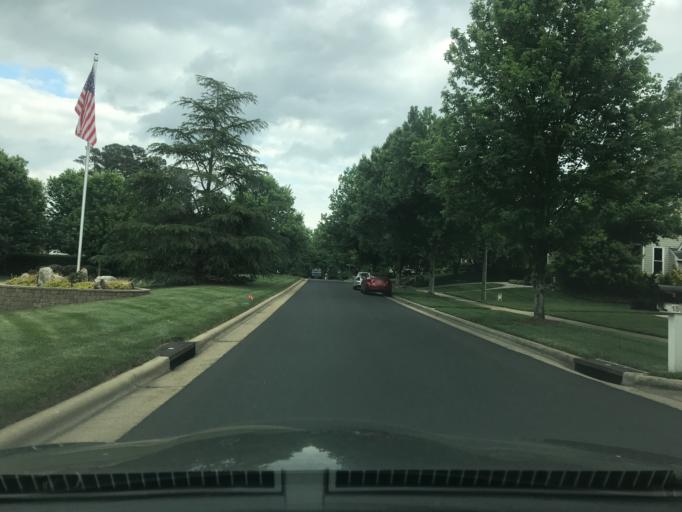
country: US
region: North Carolina
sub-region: Wake County
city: Wake Forest
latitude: 35.9128
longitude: -78.5835
